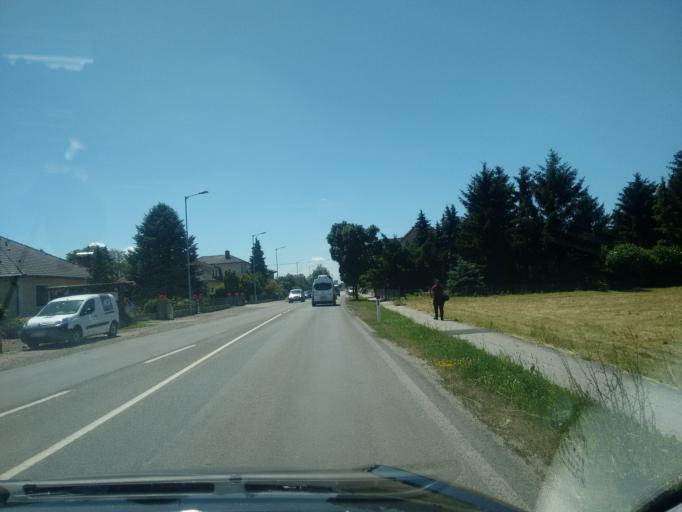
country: AT
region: Lower Austria
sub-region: Sankt Polten Stadt
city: Sankt Poelten
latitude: 48.2221
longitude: 15.6678
